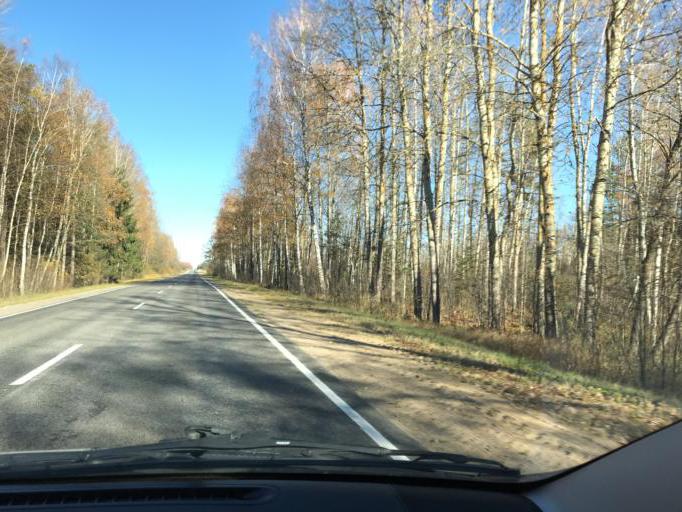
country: BY
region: Vitebsk
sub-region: Ushatski Rayon
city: Ushachy
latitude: 55.0773
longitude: 28.7548
